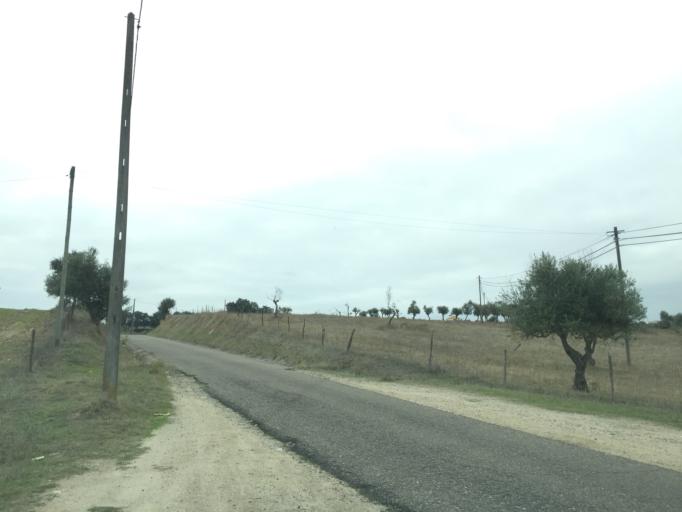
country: PT
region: Portalegre
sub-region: Avis
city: Avis
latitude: 39.0465
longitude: -7.8046
